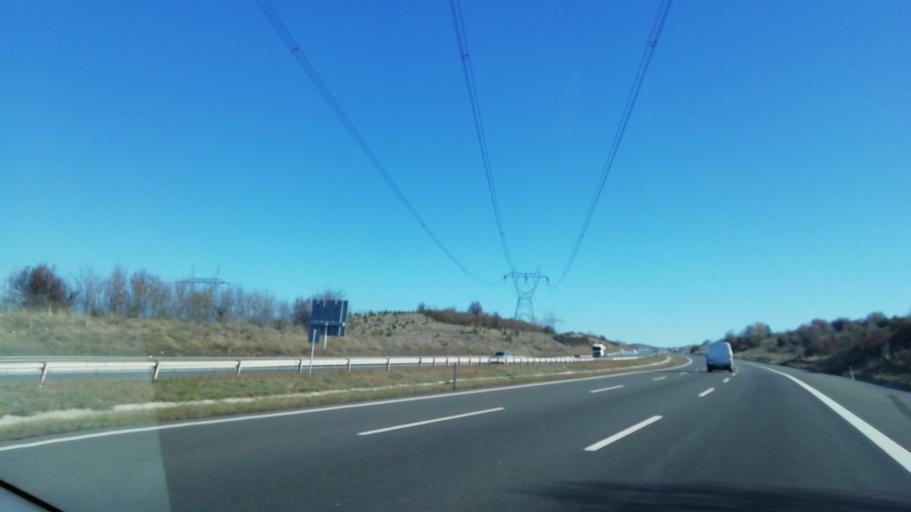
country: TR
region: Bolu
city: Yenicaga
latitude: 40.7645
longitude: 32.0391
